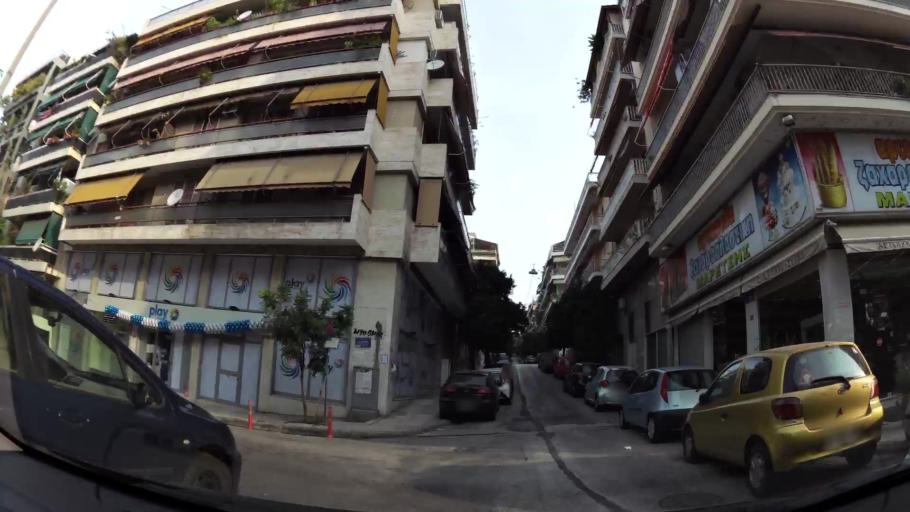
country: GR
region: Attica
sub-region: Nomarchia Athinas
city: Kipseli
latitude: 37.9928
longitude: 23.7466
